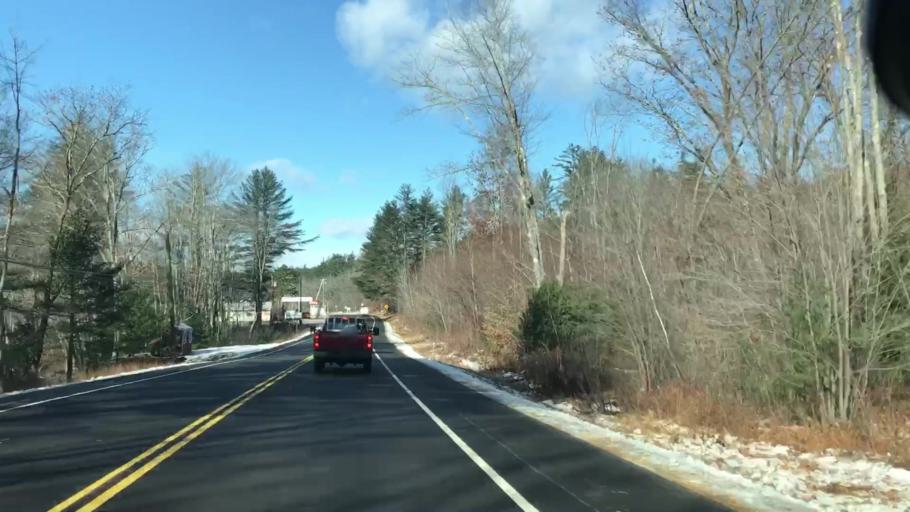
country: US
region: New Hampshire
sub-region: Carroll County
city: Effingham
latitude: 43.7948
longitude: -70.9965
